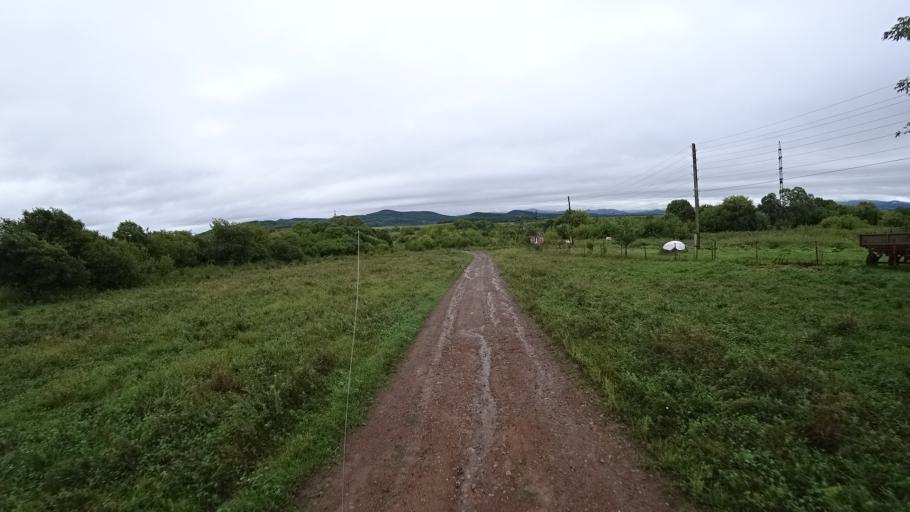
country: RU
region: Primorskiy
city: Monastyrishche
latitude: 44.2640
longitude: 132.4219
